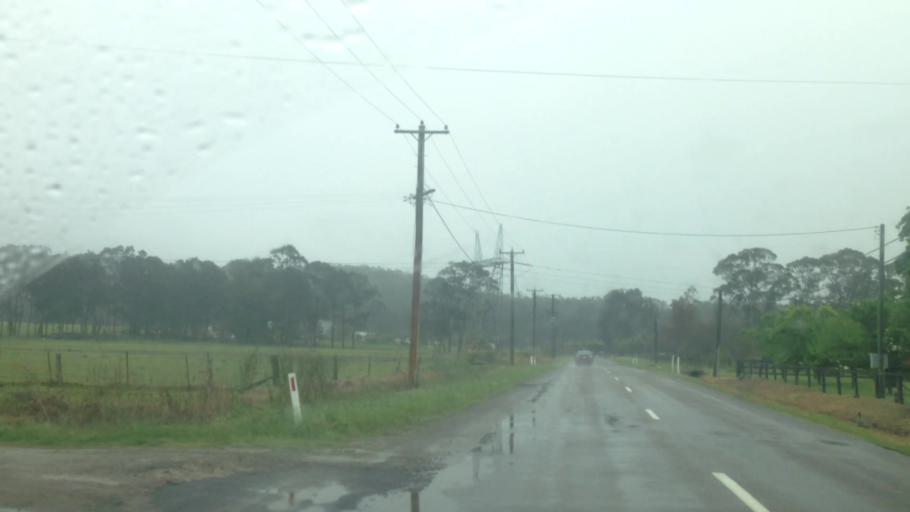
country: AU
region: New South Wales
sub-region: Wyong Shire
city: Little Jilliby
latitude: -33.2199
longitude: 151.3726
